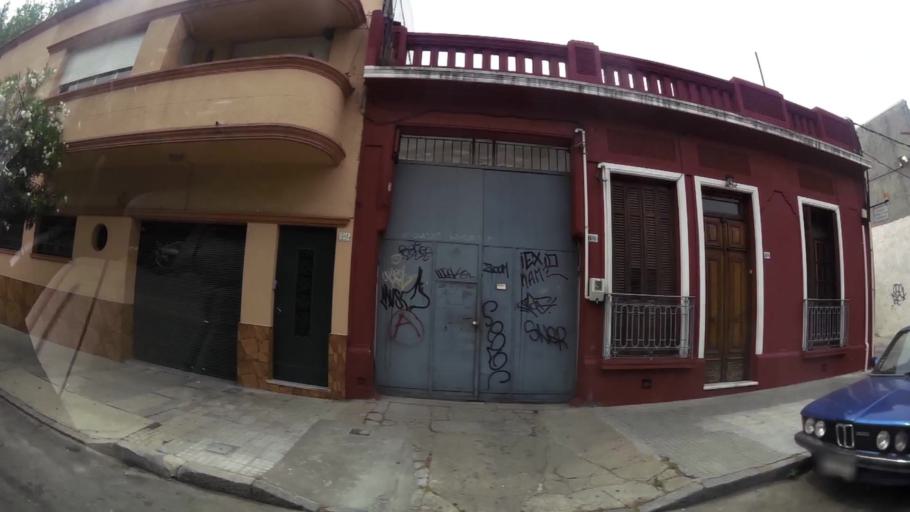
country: UY
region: Montevideo
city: Montevideo
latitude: -34.8972
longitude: -56.1762
